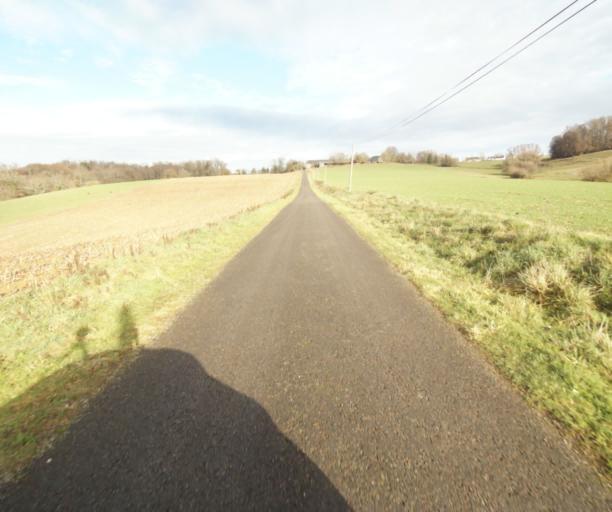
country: FR
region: Limousin
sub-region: Departement de la Correze
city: Sainte-Fereole
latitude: 45.2761
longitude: 1.5973
